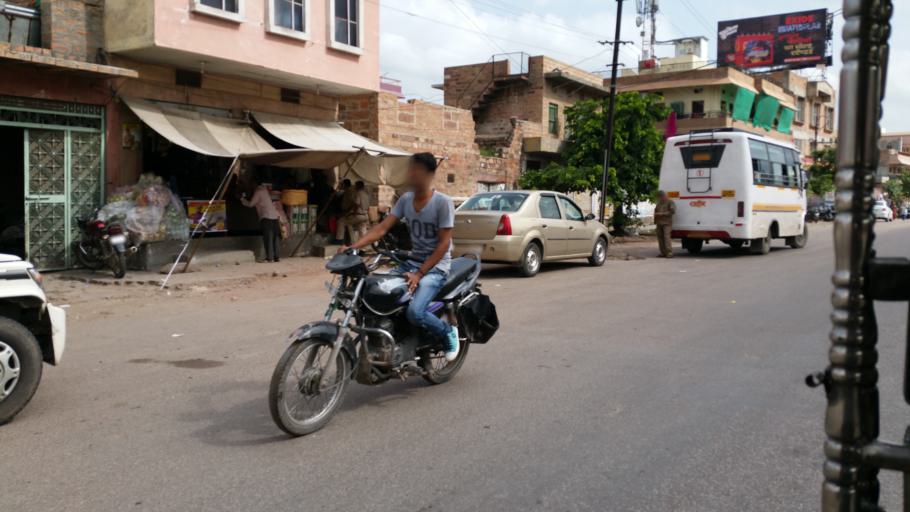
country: IN
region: Rajasthan
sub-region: Jodhpur
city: Jodhpur
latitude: 26.3204
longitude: 73.0451
